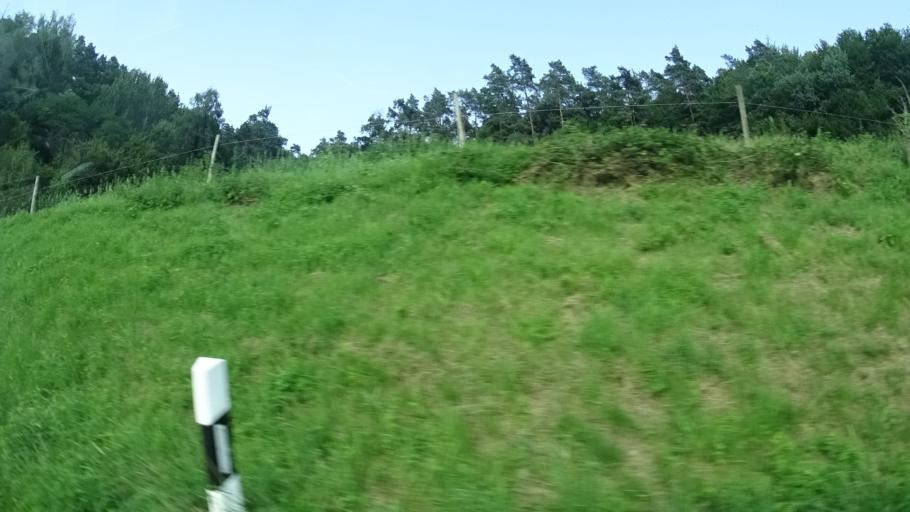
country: DE
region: Hesse
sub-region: Regierungsbezirk Darmstadt
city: Rothenberg
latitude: 49.5485
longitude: 8.9025
